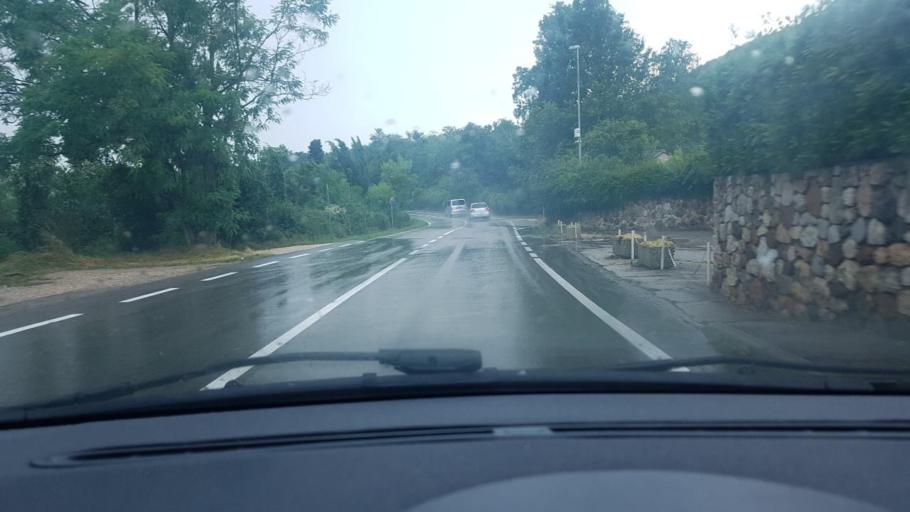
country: IT
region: Veneto
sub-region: Provincia di Verona
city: Garda
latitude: 45.5997
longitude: 10.7195
